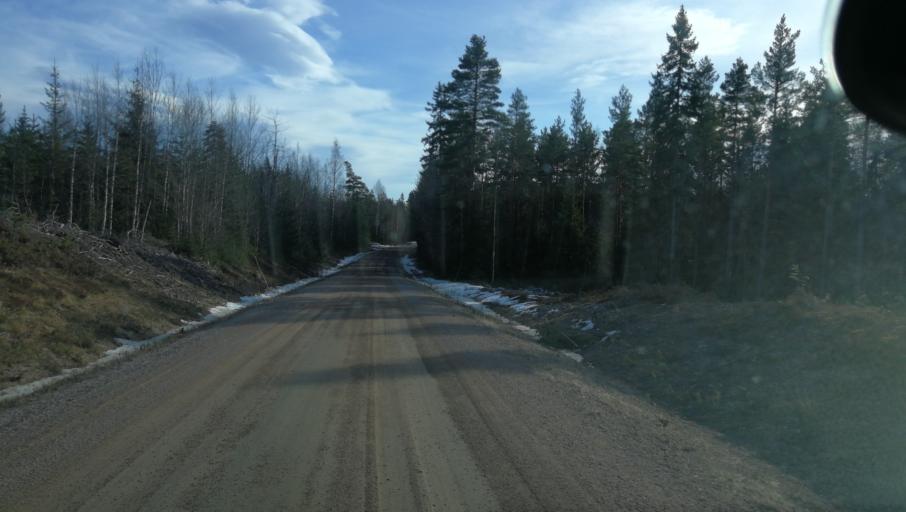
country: SE
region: Dalarna
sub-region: Vansbro Kommun
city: Vansbro
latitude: 60.8242
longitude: 14.1943
